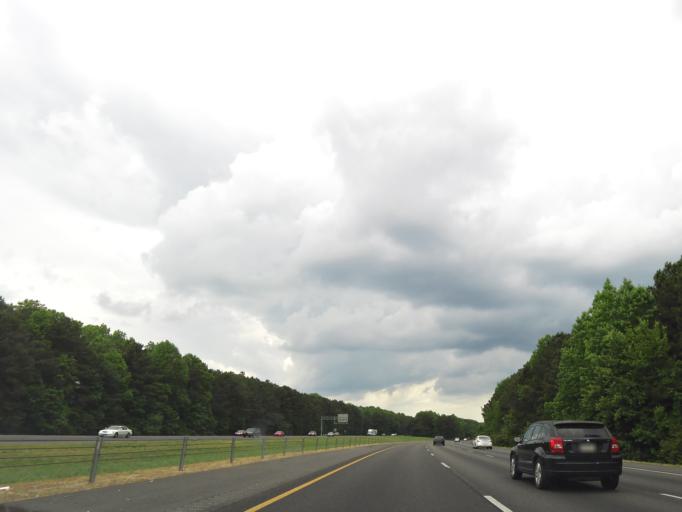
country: US
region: Georgia
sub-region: Douglas County
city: Douglasville
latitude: 33.7229
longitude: -84.7789
